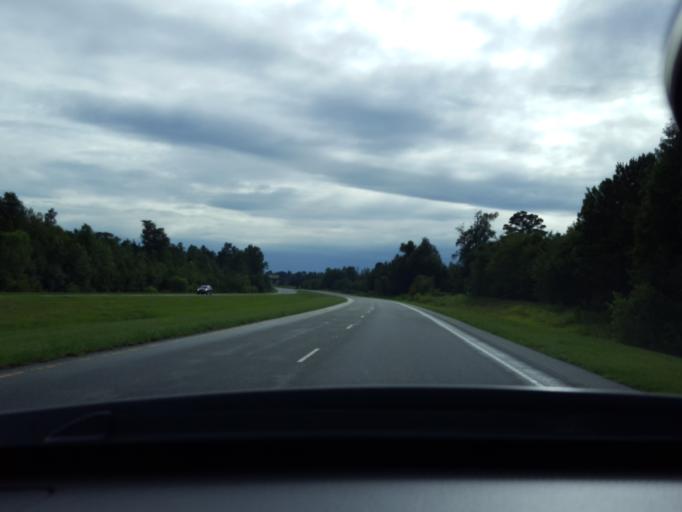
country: US
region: North Carolina
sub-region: Duplin County
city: Kenansville
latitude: 34.9273
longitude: -78.0118
